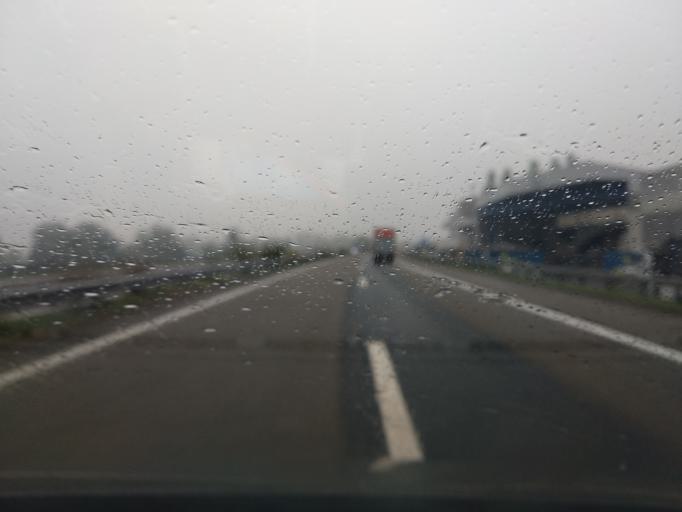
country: CH
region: Saint Gallen
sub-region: Wahlkreis Wil
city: Uzwil
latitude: 47.4520
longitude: 9.1457
